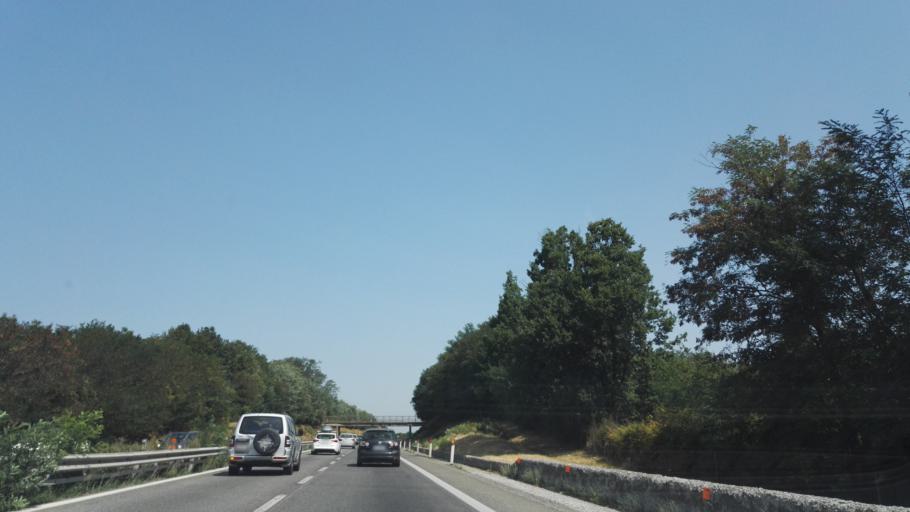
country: IT
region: Calabria
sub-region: Provincia di Cosenza
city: Figline Vegliaturo
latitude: 39.2144
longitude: 16.3062
